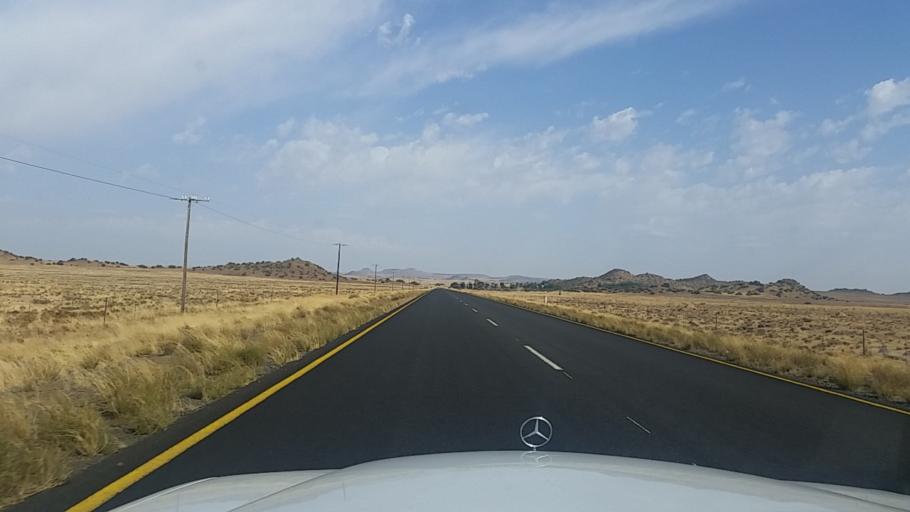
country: ZA
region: Orange Free State
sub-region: Xhariep District Municipality
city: Trompsburg
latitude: -30.3197
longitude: 25.7658
